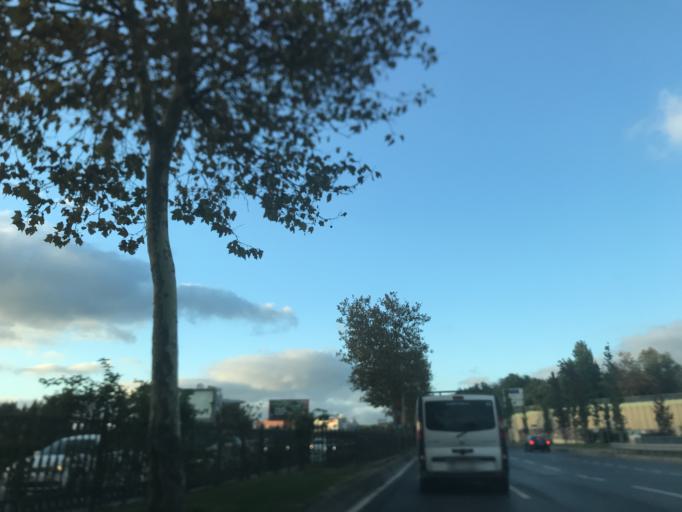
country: TR
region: Istanbul
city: Sisli
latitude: 41.1155
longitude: 29.0246
